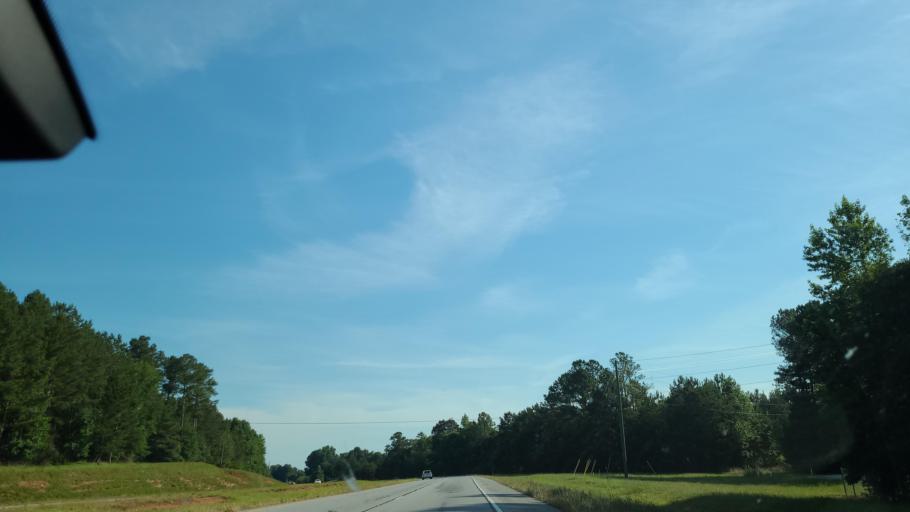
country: US
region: Georgia
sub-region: Jackson County
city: Nicholson
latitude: 34.0746
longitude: -83.4231
